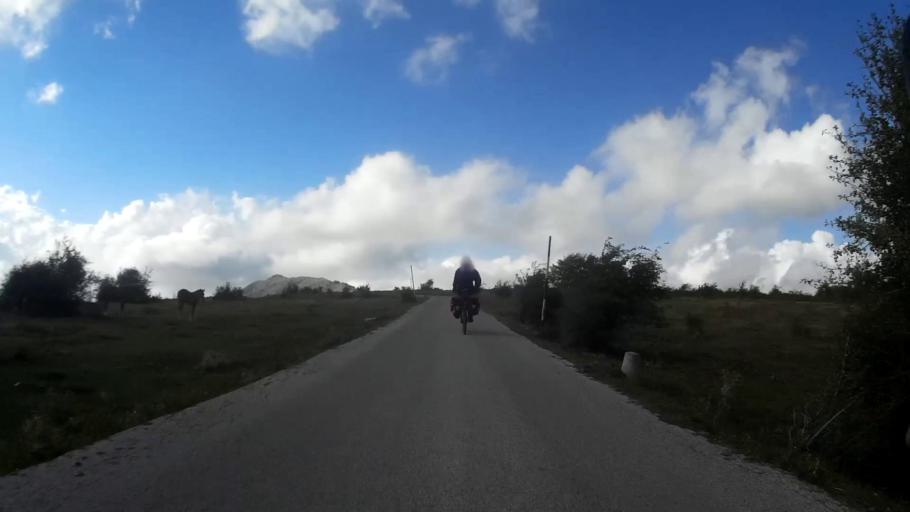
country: IT
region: Basilicate
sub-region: Provincia di Potenza
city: Viggianello
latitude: 39.9503
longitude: 16.1450
